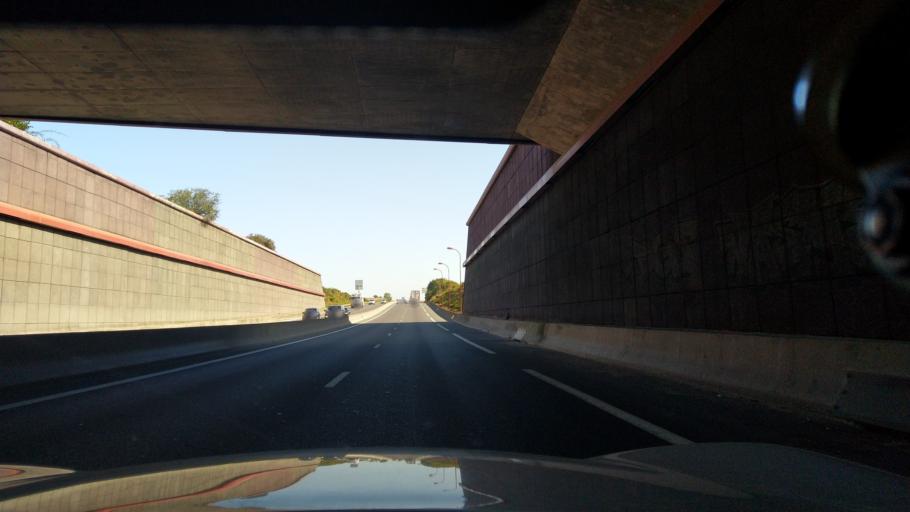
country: FR
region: Ile-de-France
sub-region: Departement du Val-d'Oise
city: Gonesse
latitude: 48.9833
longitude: 2.4691
